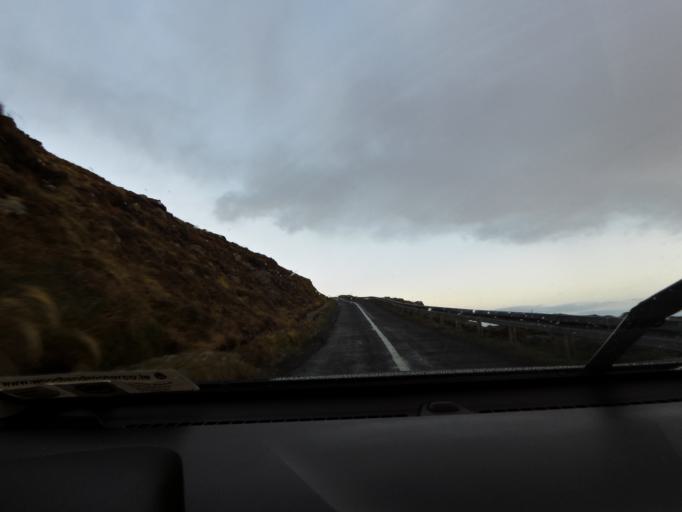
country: IE
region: Connaught
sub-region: Maigh Eo
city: Belmullet
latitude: 53.9706
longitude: -10.1852
